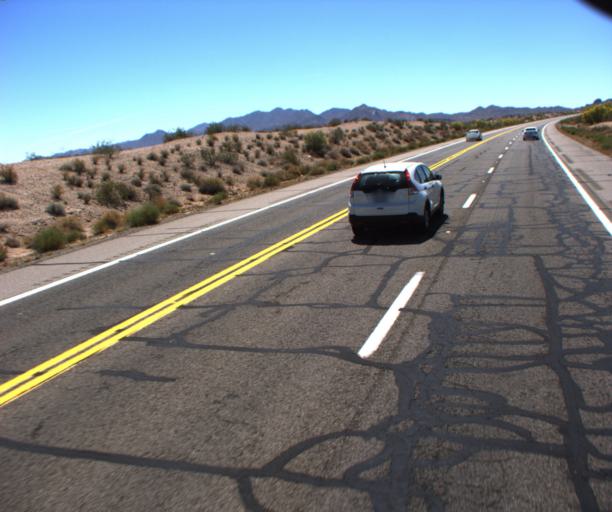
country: US
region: Arizona
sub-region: Mohave County
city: Desert Hills
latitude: 34.6978
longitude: -114.3018
